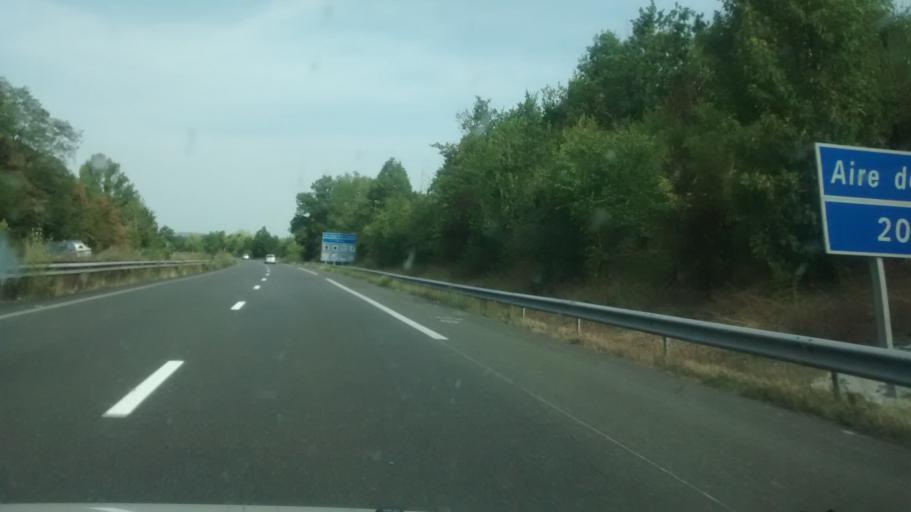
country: FR
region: Aquitaine
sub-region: Departement du Lot-et-Garonne
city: Layrac
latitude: 44.1166
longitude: 0.7245
